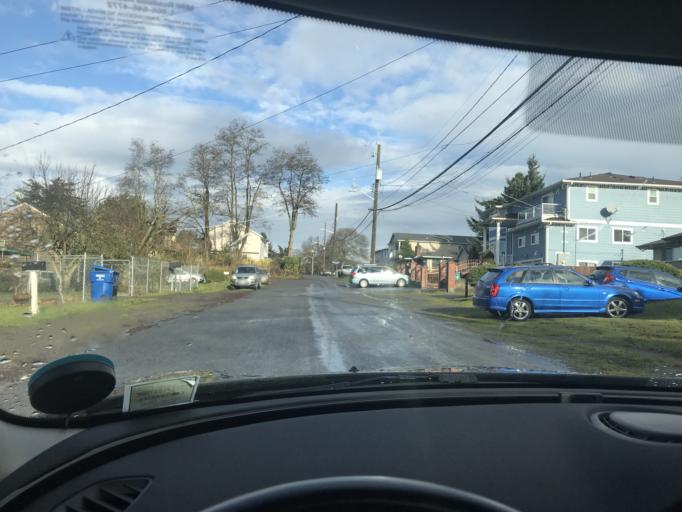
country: US
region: Washington
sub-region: King County
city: Boulevard Park
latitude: 47.5477
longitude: -122.3023
